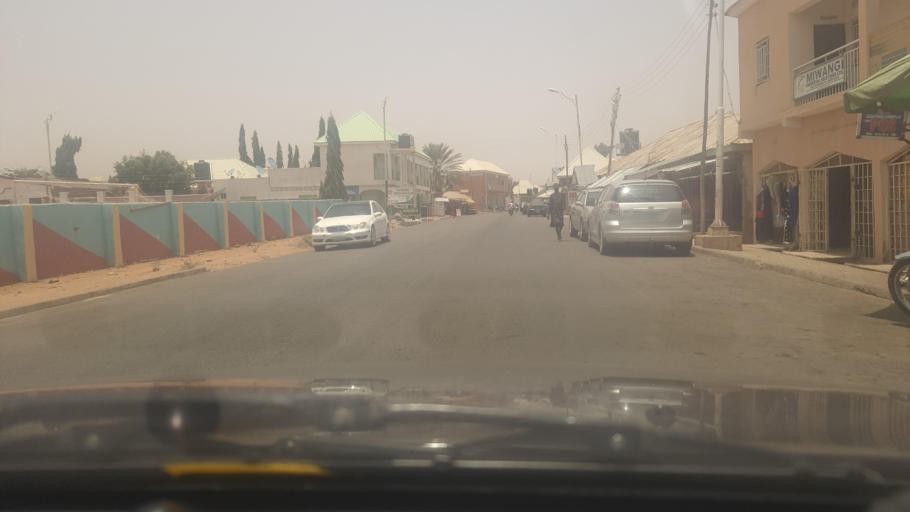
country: NG
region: Gombe
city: Gombe
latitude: 10.2997
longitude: 11.1465
